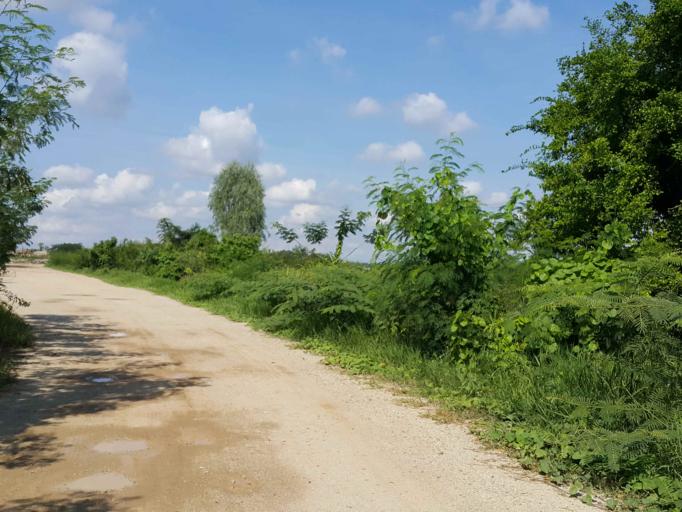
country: TH
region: Chiang Mai
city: San Kamphaeng
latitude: 18.7329
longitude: 99.0913
